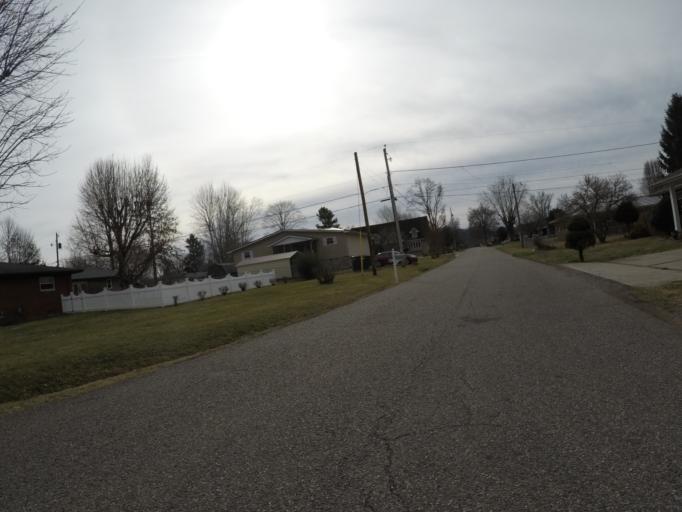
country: US
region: West Virginia
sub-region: Cabell County
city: Pea Ridge
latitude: 38.4508
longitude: -82.3530
